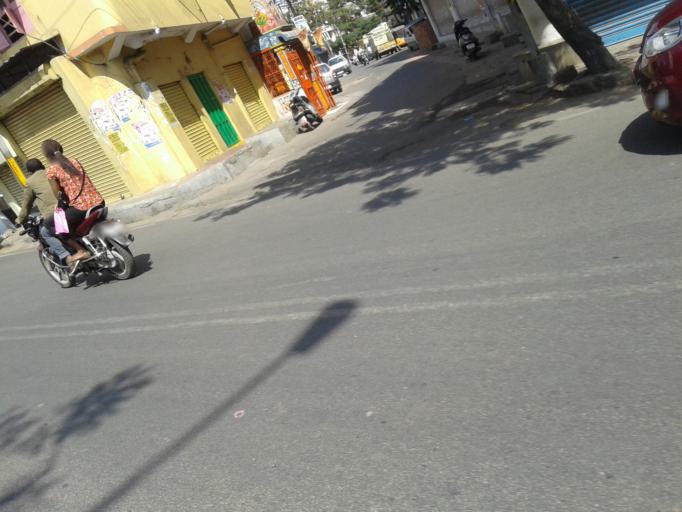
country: IN
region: Telangana
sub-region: Hyderabad
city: Hyderabad
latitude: 17.3897
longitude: 78.4856
